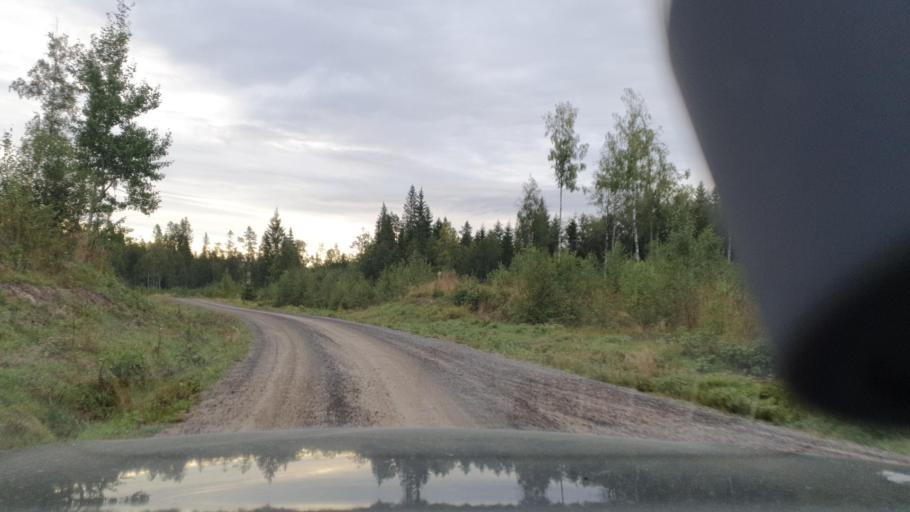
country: SE
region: Vaermland
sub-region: Sunne Kommun
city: Sunne
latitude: 59.8626
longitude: 12.8262
